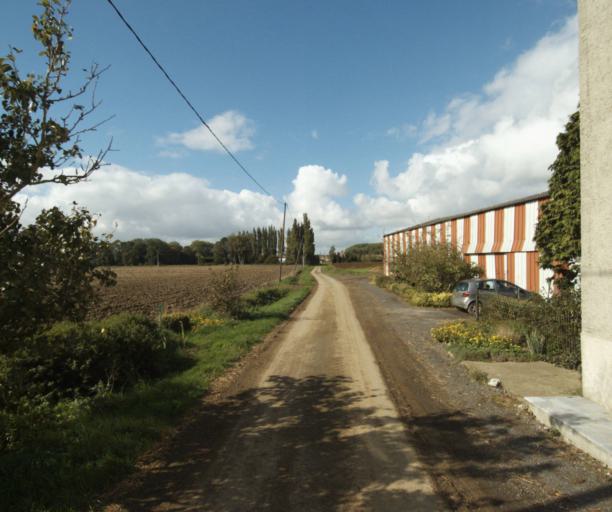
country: FR
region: Nord-Pas-de-Calais
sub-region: Departement du Nord
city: Frelinghien
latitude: 50.7154
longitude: 2.9434
